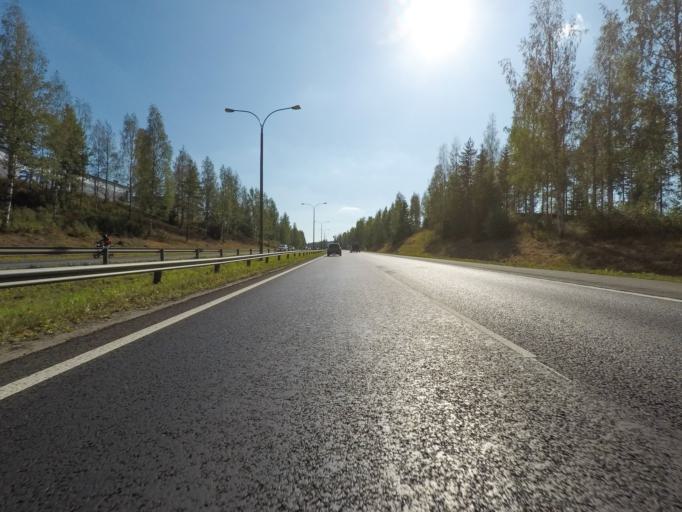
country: FI
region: Northern Savo
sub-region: Kuopio
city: Kuopio
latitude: 62.8695
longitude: 27.6192
